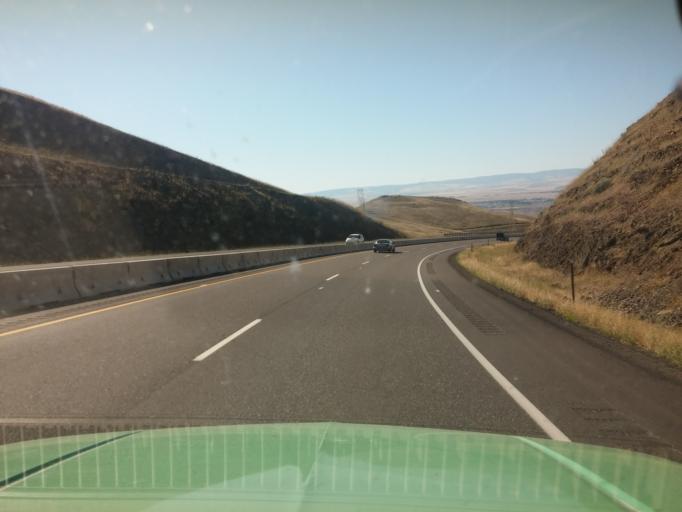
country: US
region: Idaho
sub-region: Nez Perce County
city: Lewiston
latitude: 46.4599
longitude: -116.9592
